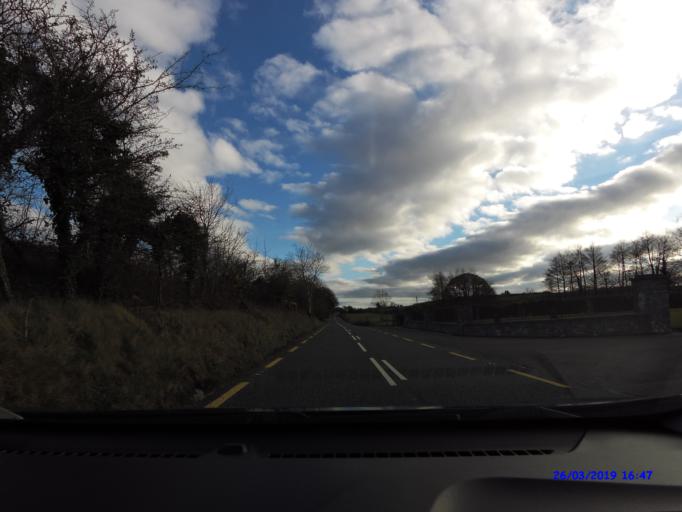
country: IE
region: Connaught
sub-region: Maigh Eo
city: Ballyhaunis
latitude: 53.8211
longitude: -8.7637
